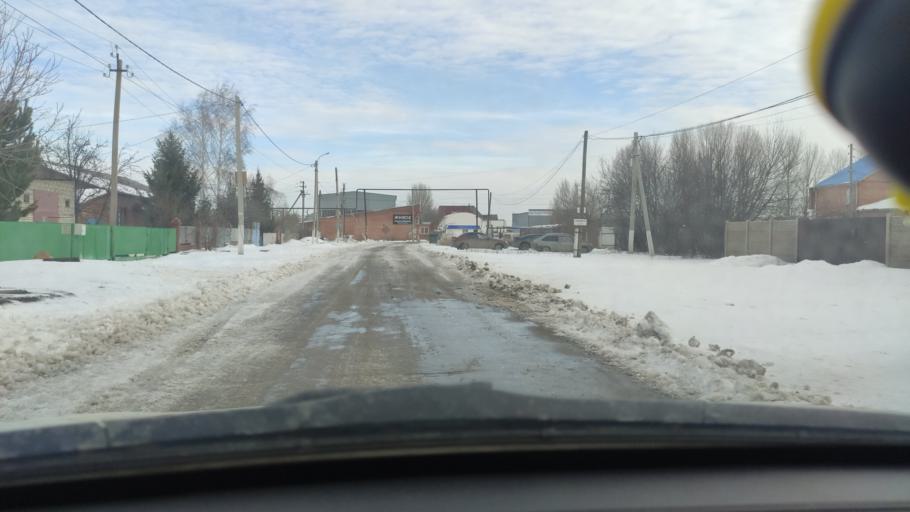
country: RU
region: Samara
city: Tol'yatti
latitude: 53.5684
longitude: 49.3906
